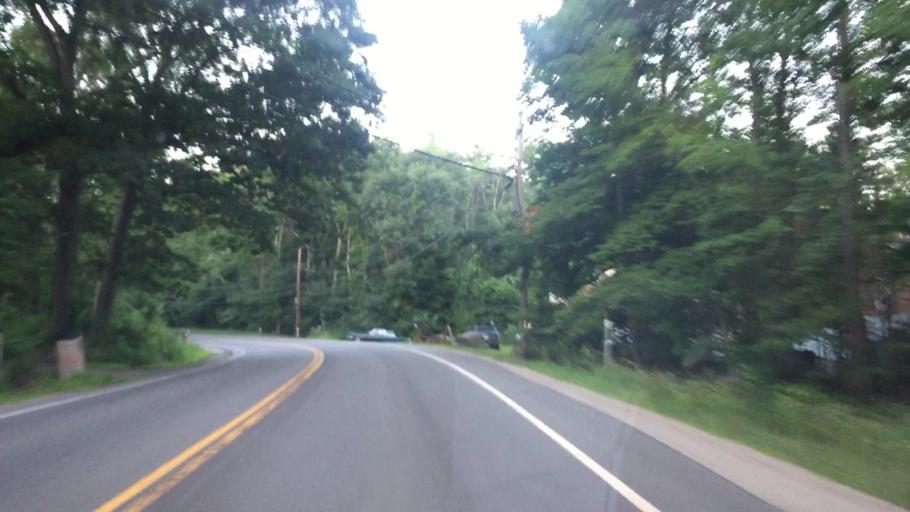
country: US
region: Massachusetts
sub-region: Middlesex County
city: Tyngsboro
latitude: 42.7017
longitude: -71.3836
